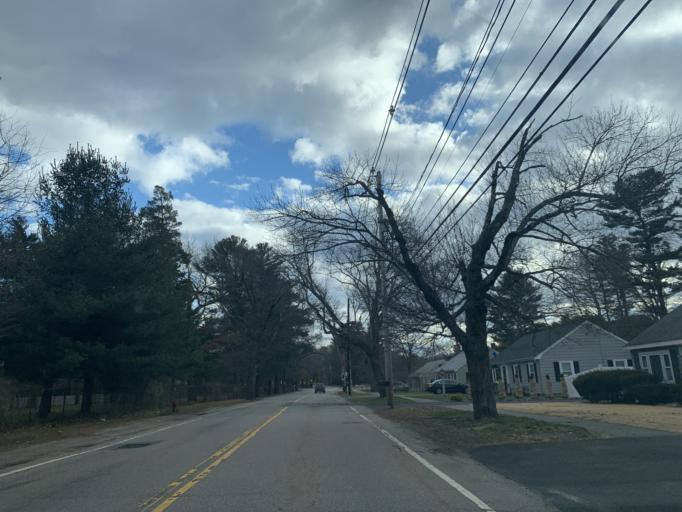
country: US
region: Massachusetts
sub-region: Norfolk County
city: Canton
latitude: 42.1775
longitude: -71.1425
